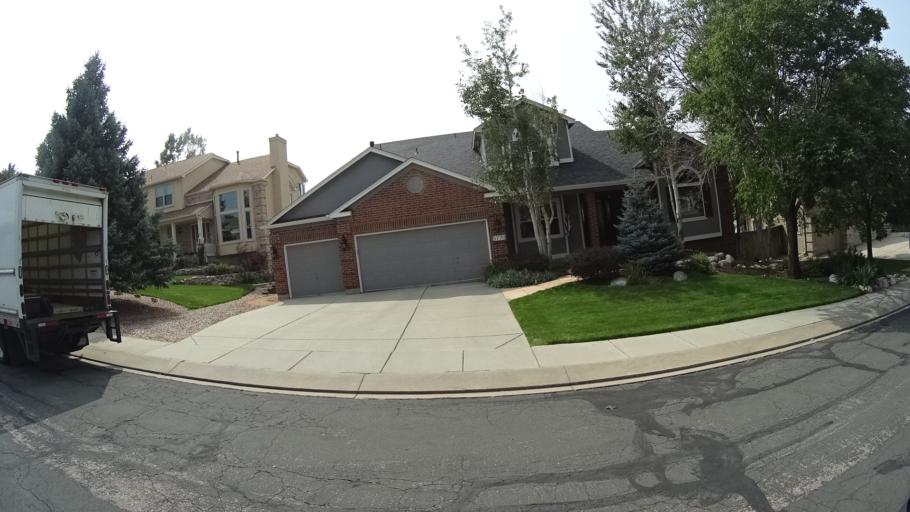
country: US
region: Colorado
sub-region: El Paso County
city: Cimarron Hills
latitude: 38.9151
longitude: -104.7455
